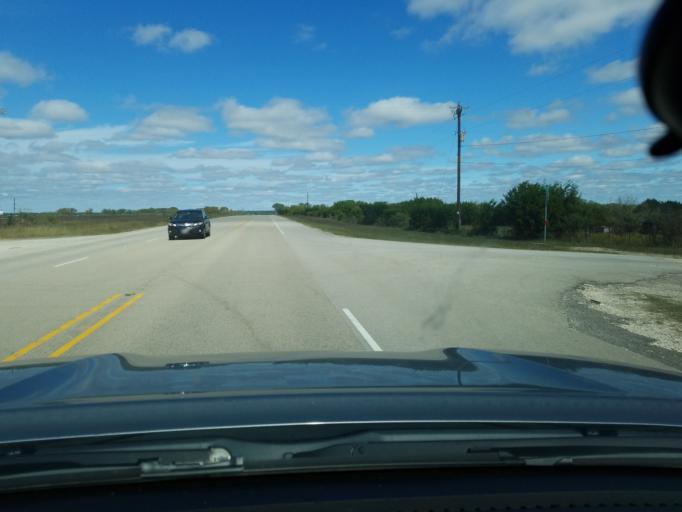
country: US
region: Texas
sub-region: Hamilton County
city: Hamilton
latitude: 31.5694
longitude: -98.1583
